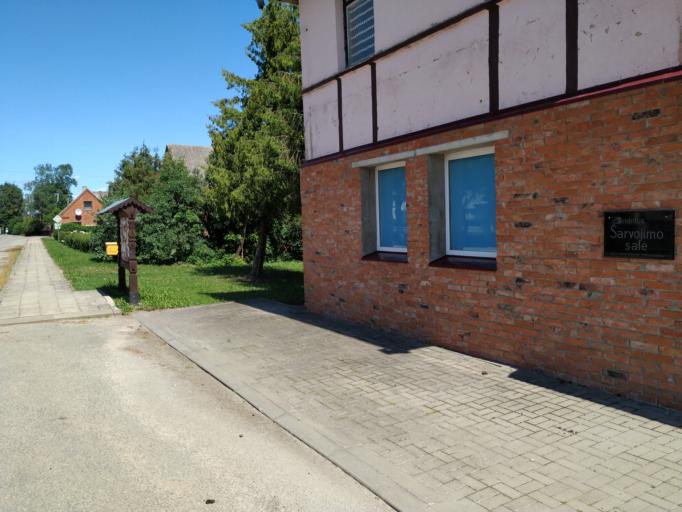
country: LT
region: Panevezys
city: Pasvalys
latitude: 56.2277
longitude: 24.4043
